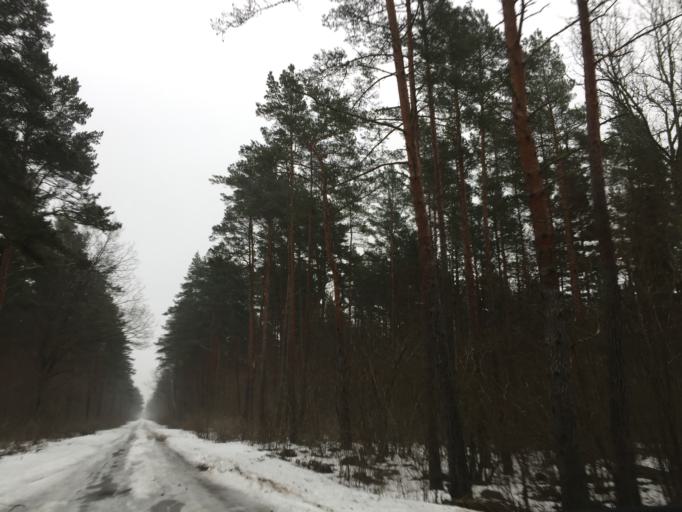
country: EE
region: Saare
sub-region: Kuressaare linn
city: Kuressaare
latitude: 58.2694
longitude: 22.5487
